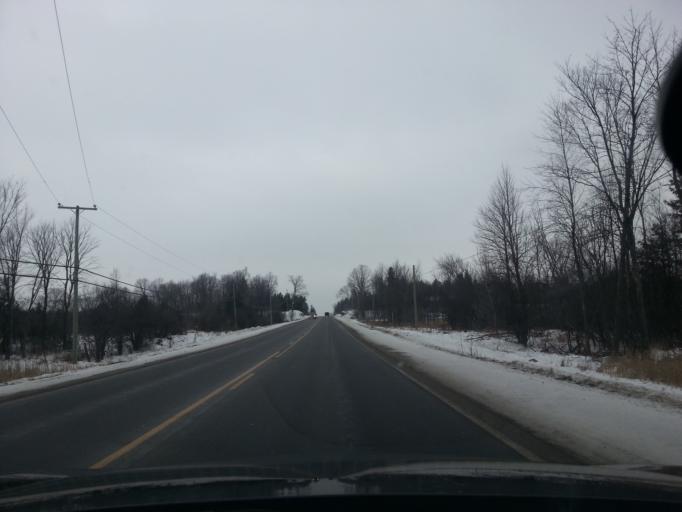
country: CA
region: Ontario
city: Carleton Place
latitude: 45.2432
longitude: -76.1692
